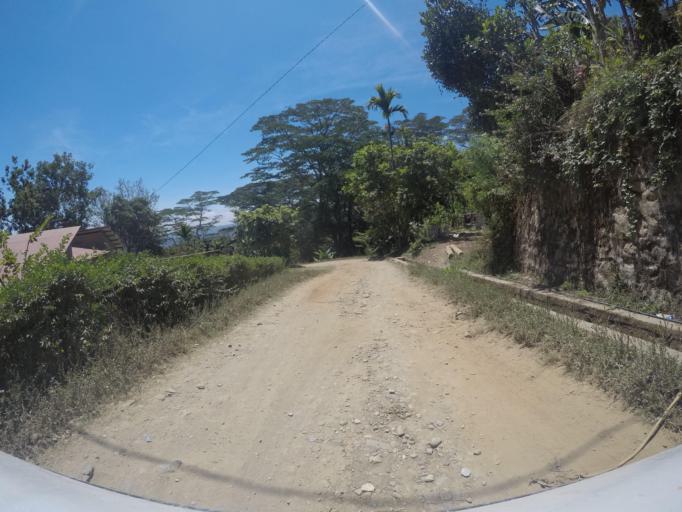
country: TL
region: Ermera
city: Gleno
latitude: -8.7392
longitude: 125.4073
